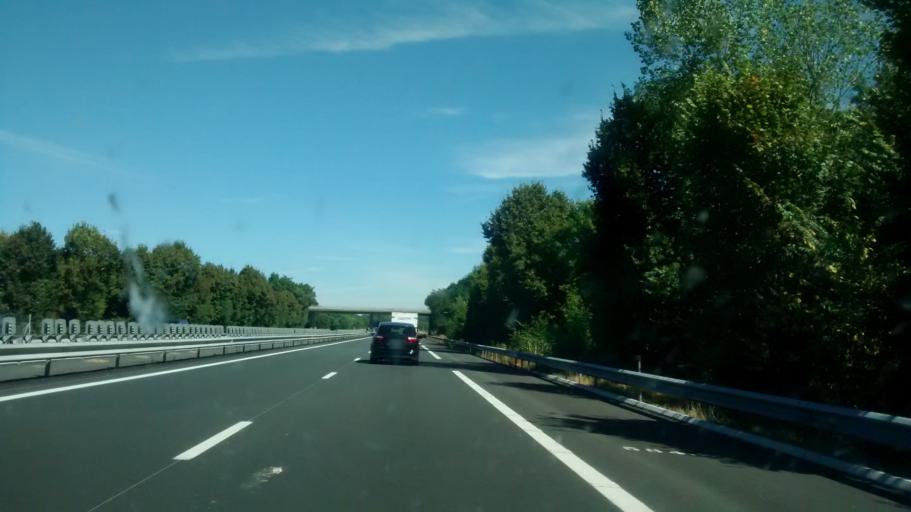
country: FR
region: Poitou-Charentes
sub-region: Departement des Deux-Sevres
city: Beauvoir-sur-Niort
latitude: 46.2060
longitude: -0.4684
